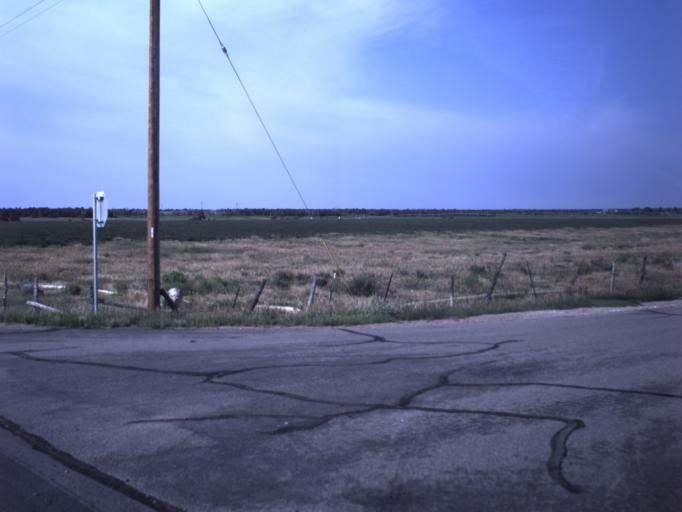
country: US
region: Utah
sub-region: Duchesne County
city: Duchesne
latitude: 40.3400
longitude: -110.4079
